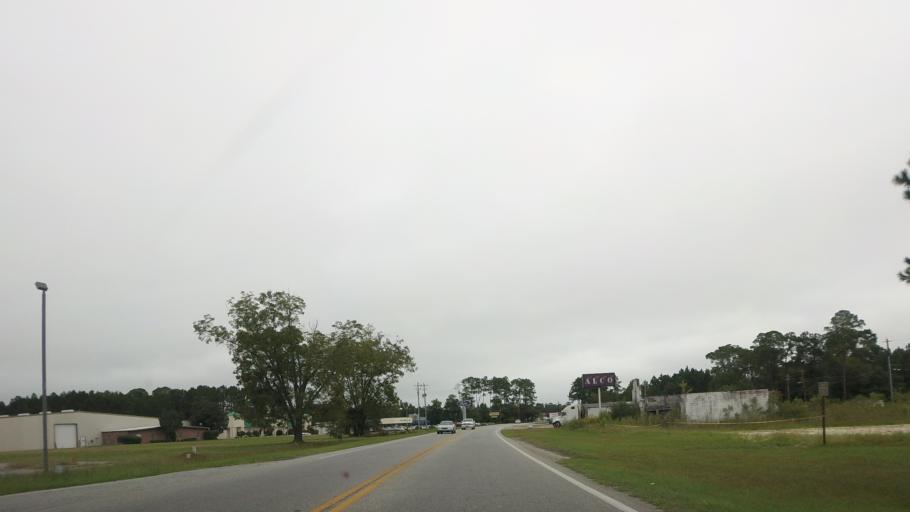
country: US
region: Georgia
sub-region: Berrien County
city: Nashville
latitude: 31.1941
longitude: -83.2510
